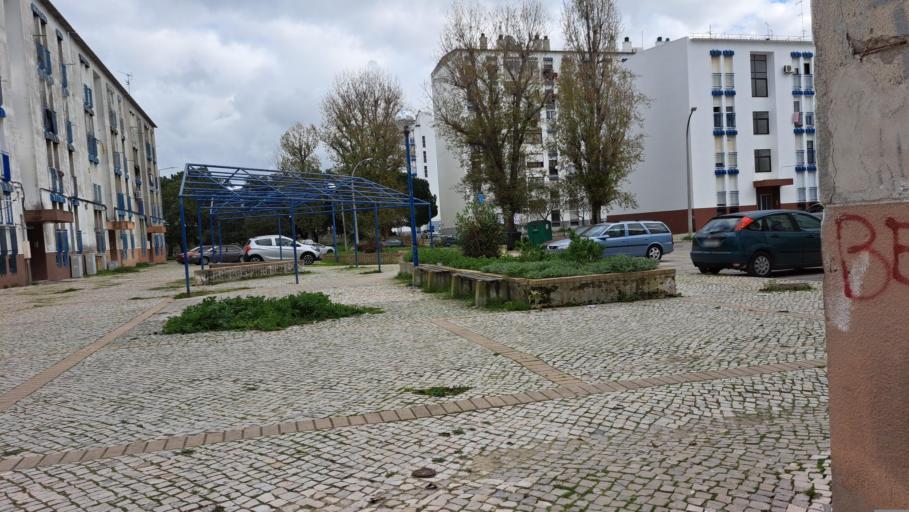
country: PT
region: Setubal
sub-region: Moita
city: Alhos Vedros
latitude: 38.6495
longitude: -9.0373
